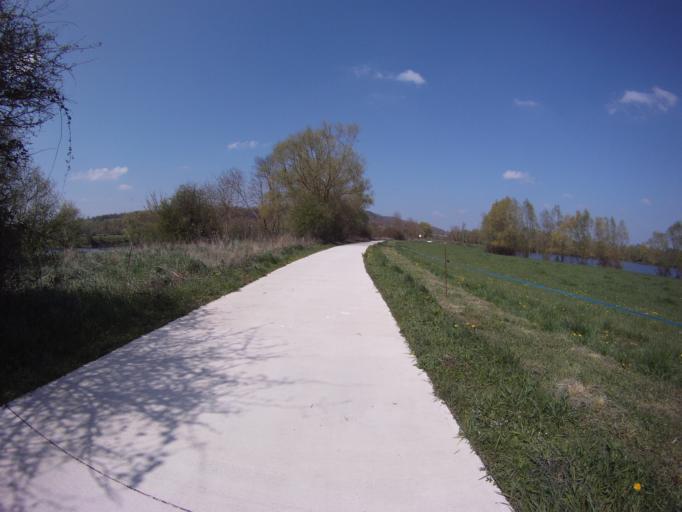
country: FR
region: Lorraine
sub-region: Departement de Meurthe-et-Moselle
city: Dieulouard
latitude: 48.8450
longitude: 6.0813
